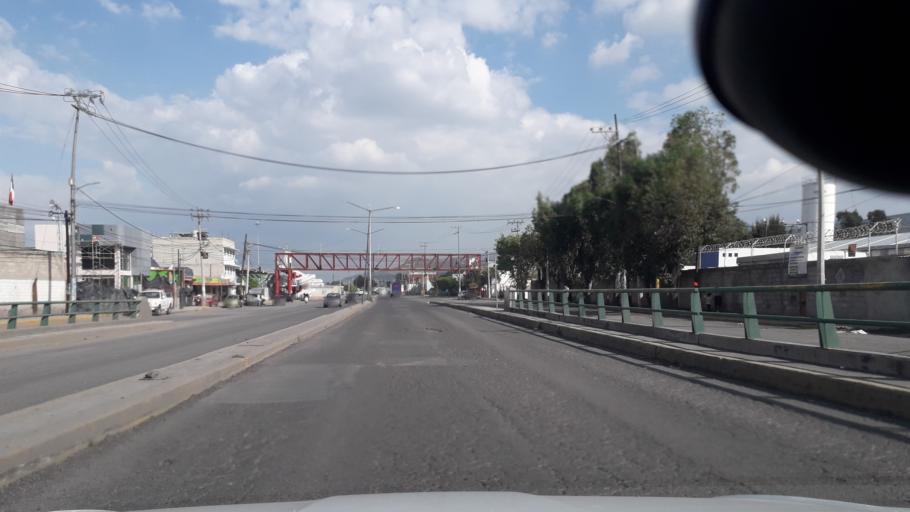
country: MX
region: Mexico
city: Tultitlan
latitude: 19.6326
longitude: -99.1785
